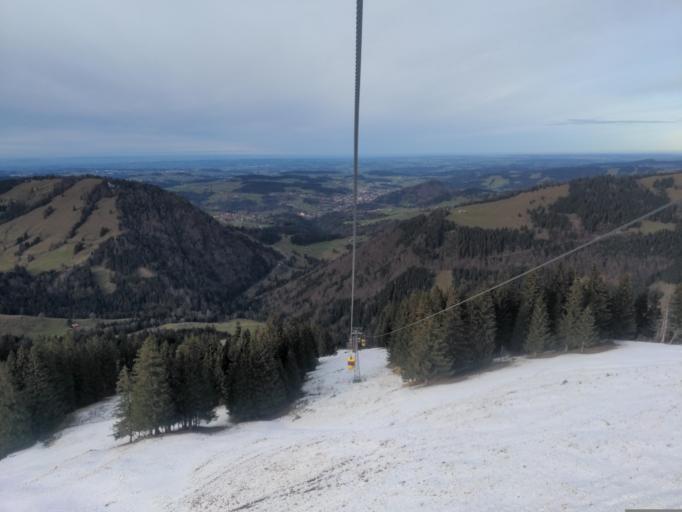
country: DE
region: Bavaria
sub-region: Swabia
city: Balderschwang
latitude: 47.4973
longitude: 10.0684
